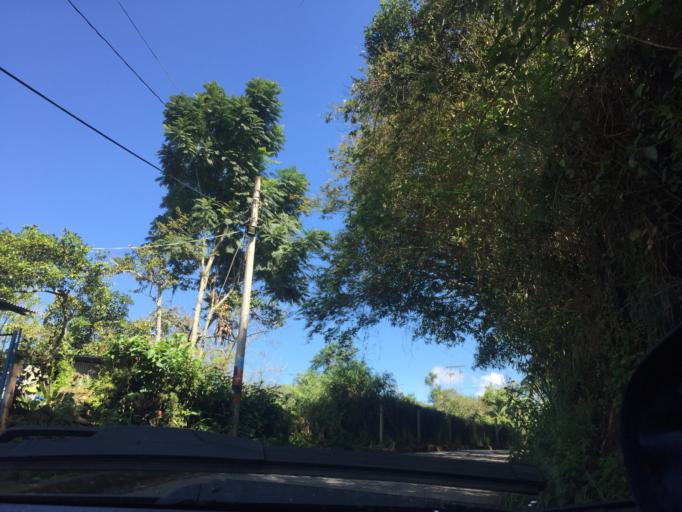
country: CO
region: Cundinamarca
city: San Francisco
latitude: 4.9821
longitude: -74.2912
